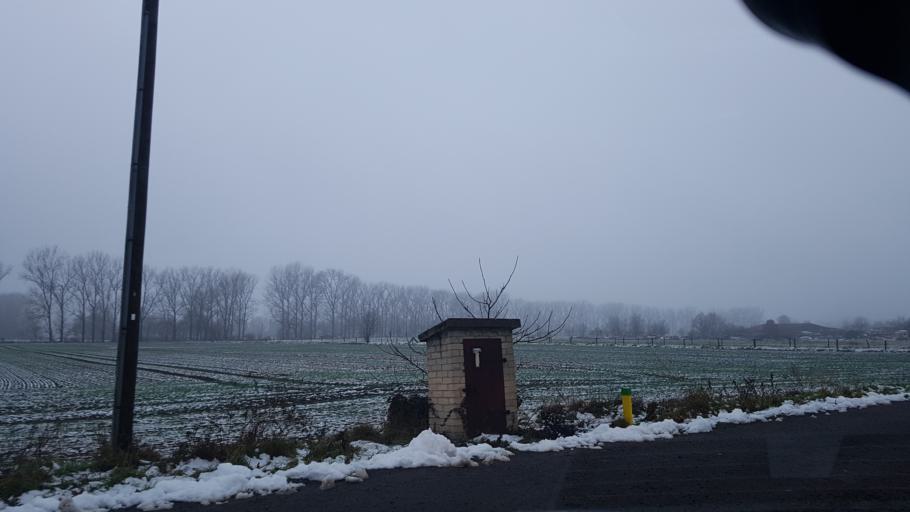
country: DE
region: Brandenburg
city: Bad Liebenwerda
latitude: 51.5196
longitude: 13.3826
